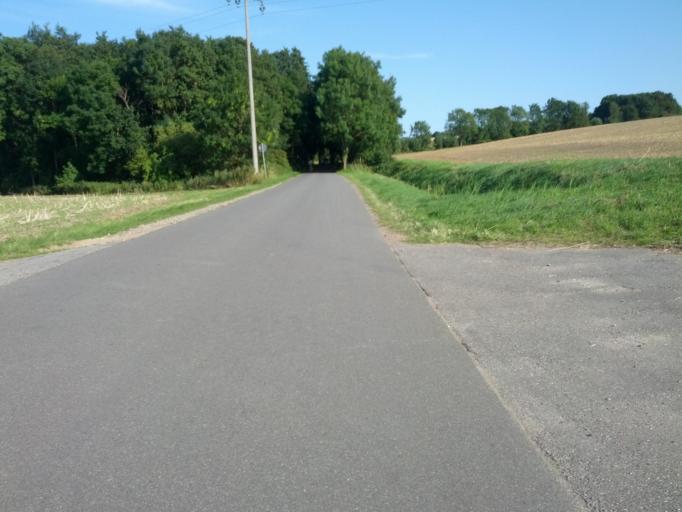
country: DE
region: Mecklenburg-Vorpommern
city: Bastorf
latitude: 54.1395
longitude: 11.6699
